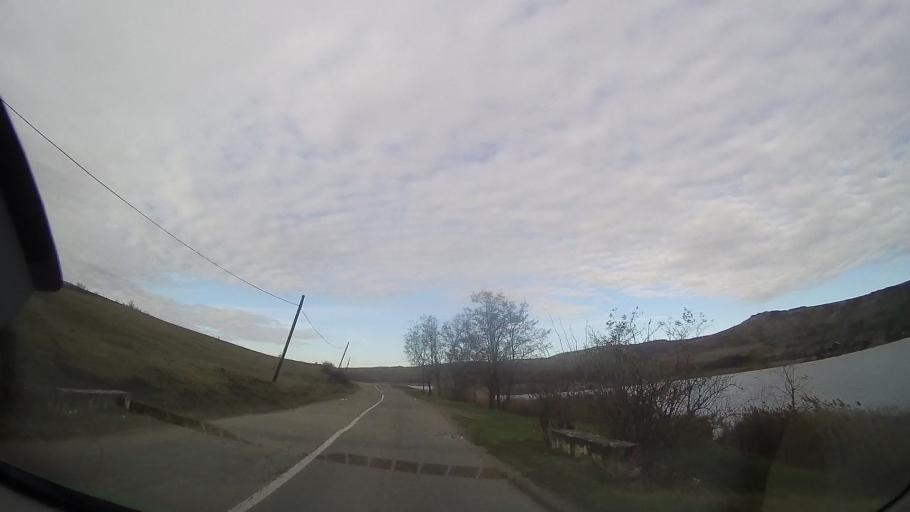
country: RO
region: Cluj
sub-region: Comuna Geaca
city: Geaca
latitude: 46.8431
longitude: 24.1232
